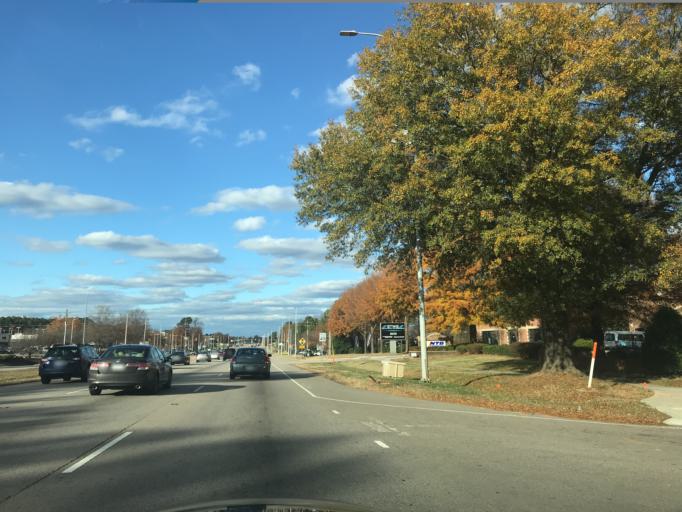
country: US
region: North Carolina
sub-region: Wake County
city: Raleigh
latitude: 35.8588
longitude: -78.5813
